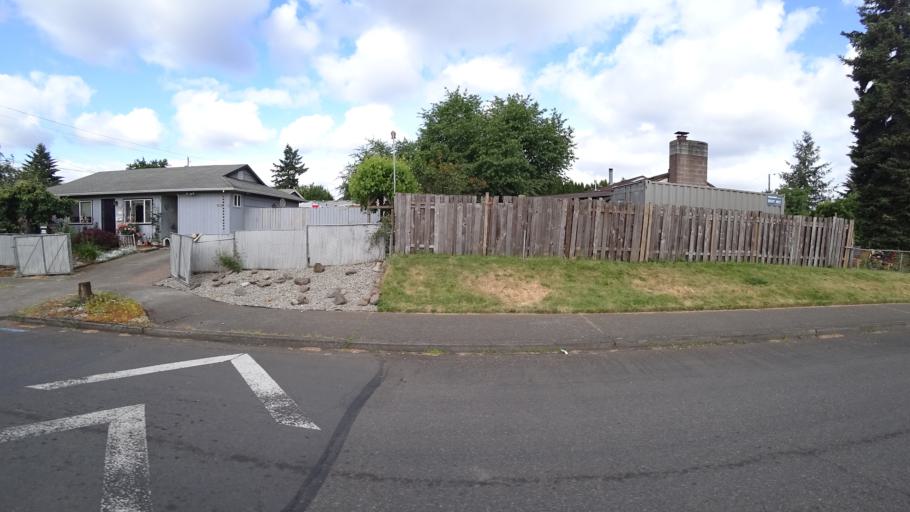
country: US
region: Oregon
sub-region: Multnomah County
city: Lents
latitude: 45.4808
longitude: -122.5597
